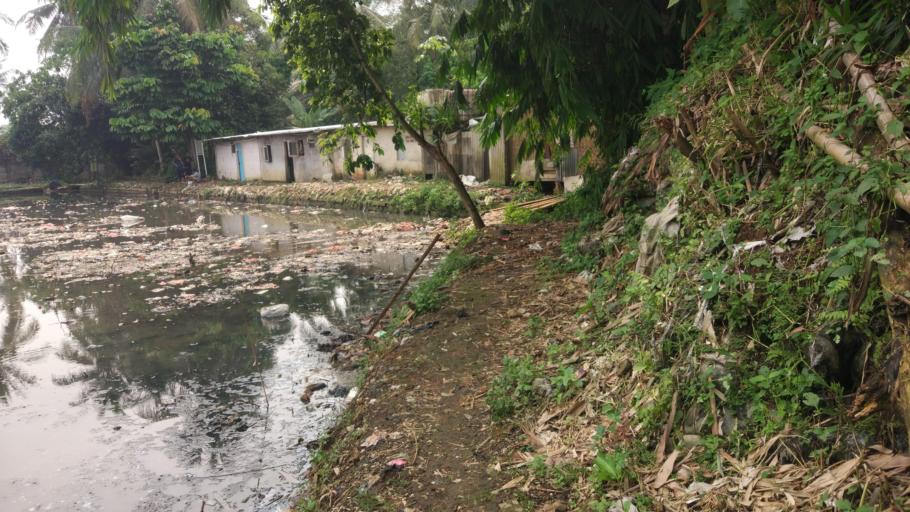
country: ID
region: West Java
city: Ciampea
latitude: -6.5650
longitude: 106.7175
